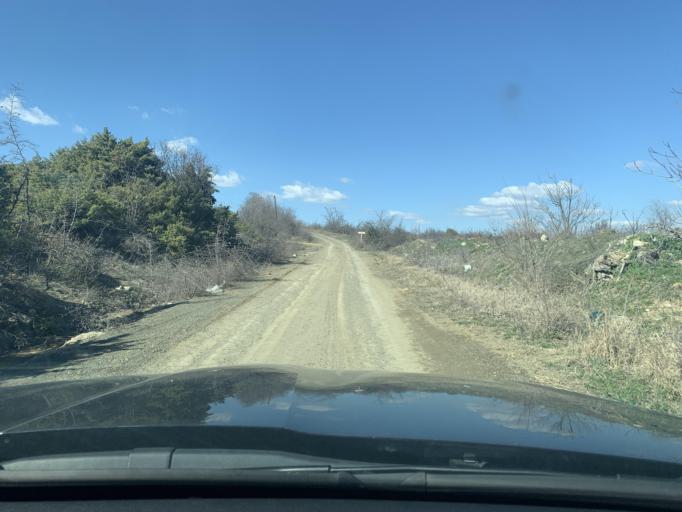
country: MK
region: Demir Kapija
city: Demir Kapija
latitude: 41.4127
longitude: 22.2238
